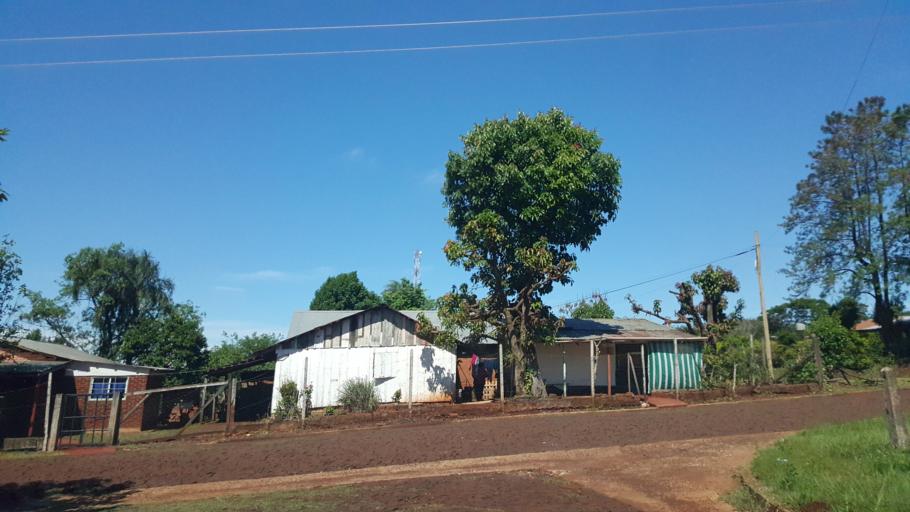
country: AR
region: Misiones
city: Capiovi
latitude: -26.9294
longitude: -55.0650
